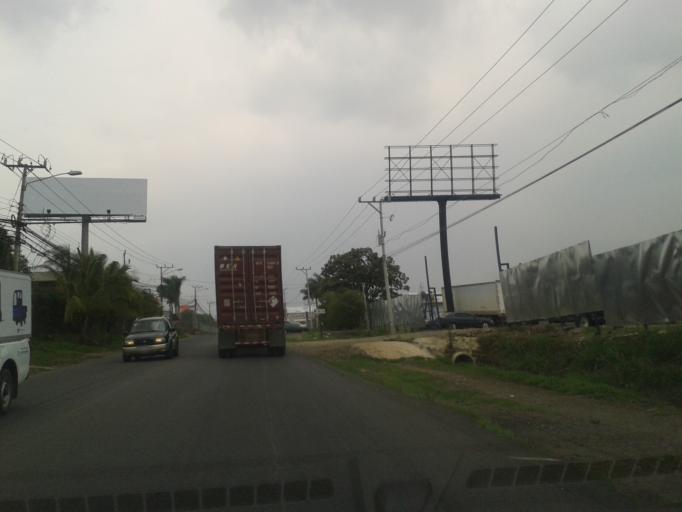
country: CR
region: Heredia
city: San Francisco
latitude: 9.9686
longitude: -84.1278
